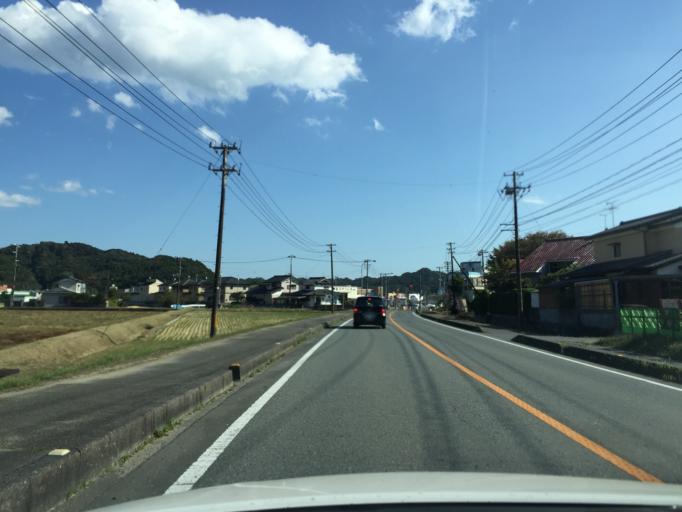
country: JP
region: Fukushima
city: Iwaki
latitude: 36.9981
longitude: 140.9027
